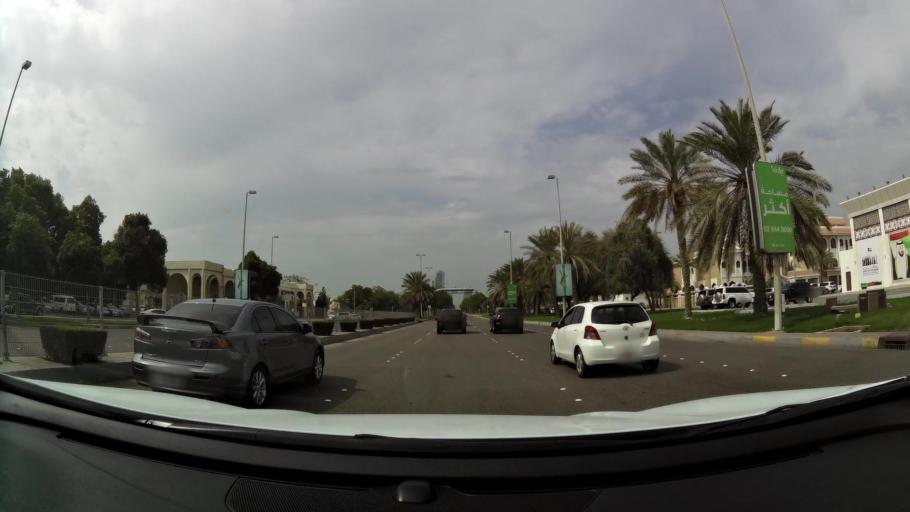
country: AE
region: Abu Dhabi
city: Abu Dhabi
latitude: 24.4622
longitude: 54.3609
